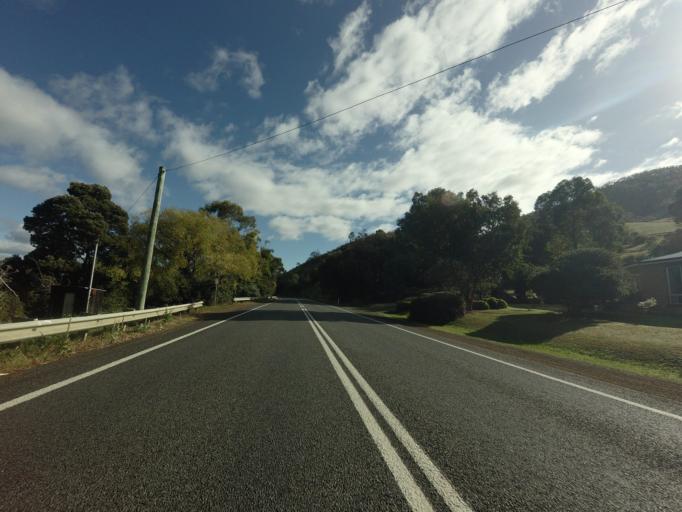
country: AU
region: Tasmania
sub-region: Derwent Valley
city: New Norfolk
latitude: -42.7282
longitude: 146.9560
